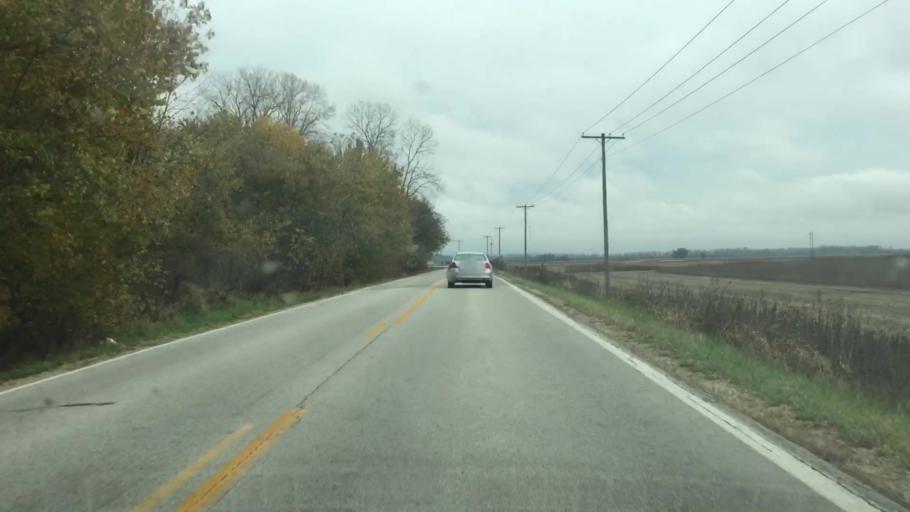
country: US
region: Missouri
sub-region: Gasconade County
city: Hermann
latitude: 38.7246
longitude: -91.4874
